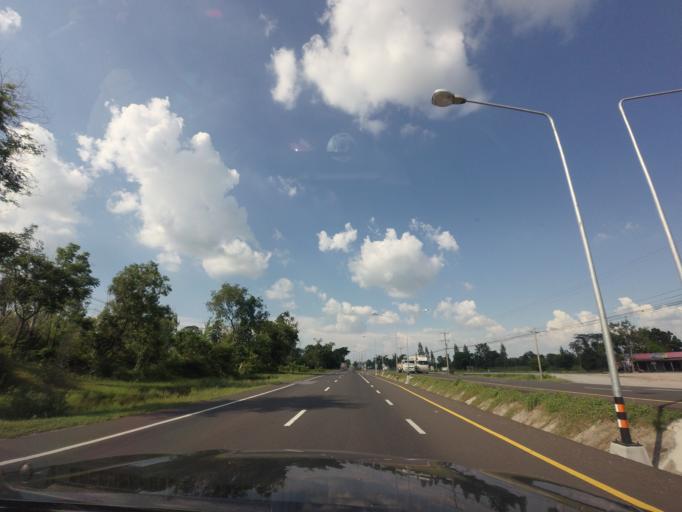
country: TH
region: Nakhon Ratchasima
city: Bua Lai
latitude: 15.7030
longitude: 102.5849
